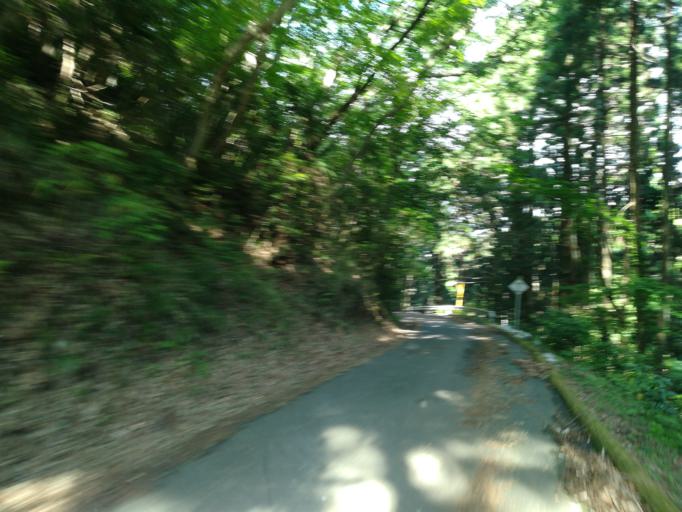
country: JP
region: Ibaraki
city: Tsukuba
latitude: 36.1848
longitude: 140.1349
